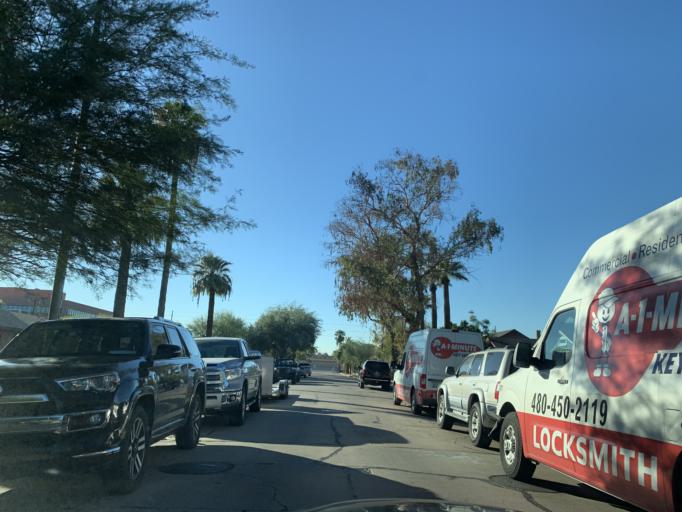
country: US
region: Arizona
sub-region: Maricopa County
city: Phoenix
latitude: 33.4672
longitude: -112.0628
